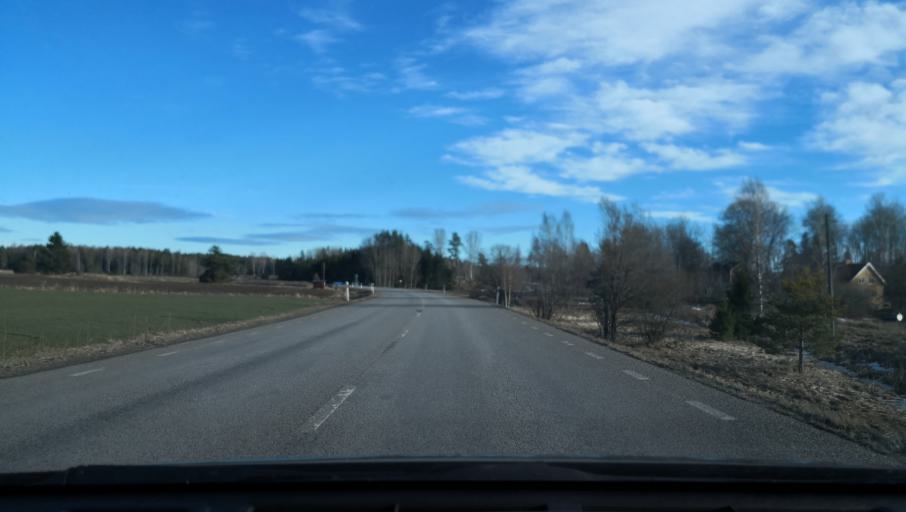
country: SE
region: Uppsala
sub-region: Osthammars Kommun
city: Osterbybruk
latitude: 60.1628
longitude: 17.9831
